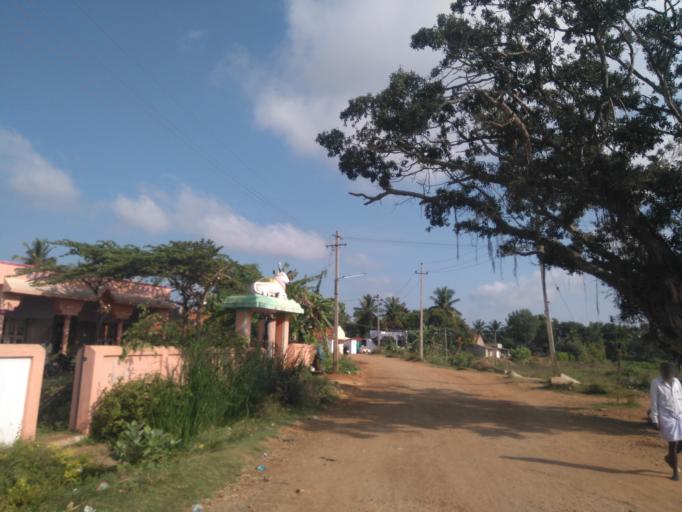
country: IN
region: Karnataka
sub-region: Mysore
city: Tirumakudal Narsipur
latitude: 12.2587
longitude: 76.9741
